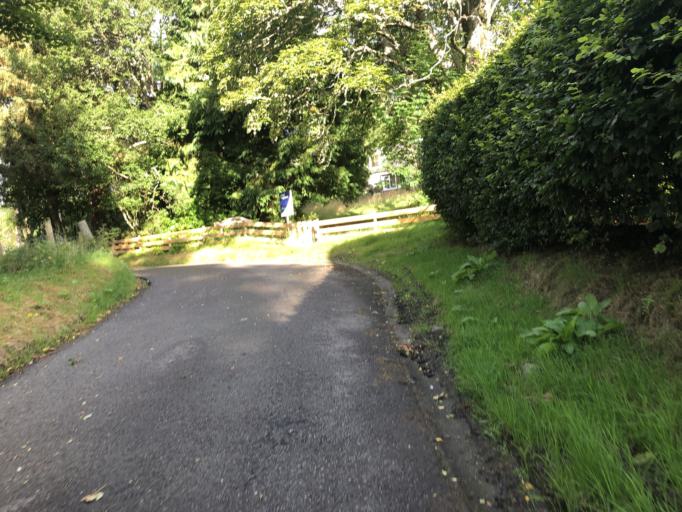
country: GB
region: Scotland
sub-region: Highland
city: Kingussie
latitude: 57.0666
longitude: -4.1280
